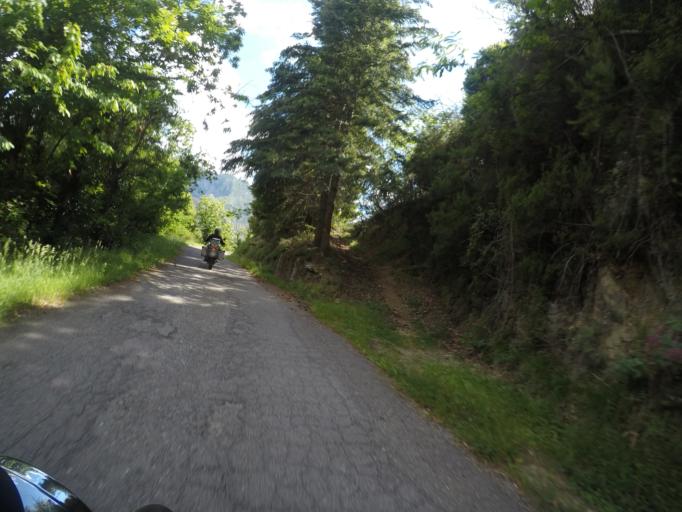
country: IT
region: Tuscany
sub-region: Provincia di Massa-Carrara
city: Casola in Lunigiana
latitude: 44.1774
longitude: 10.1598
